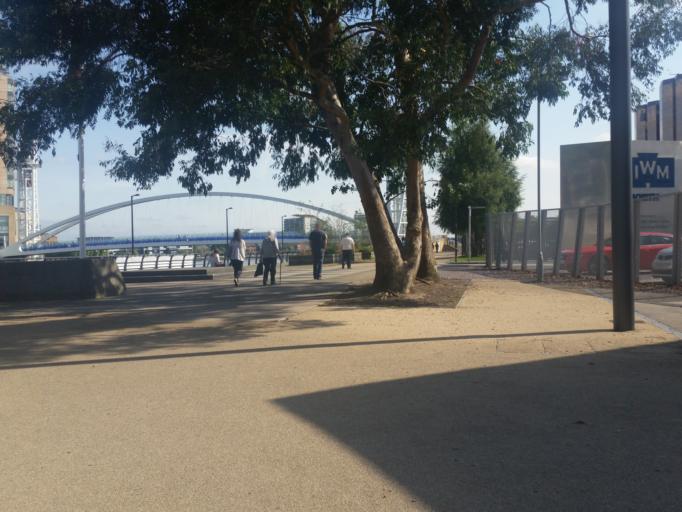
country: GB
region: England
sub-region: Trafford
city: Trafford Park
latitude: 53.4700
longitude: -2.2981
